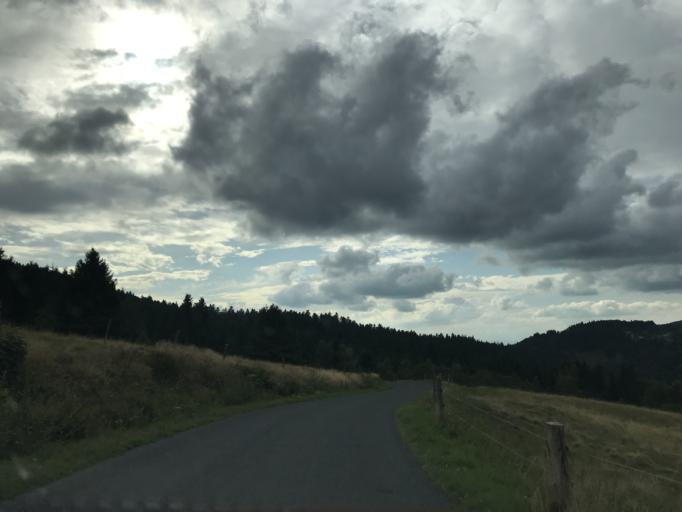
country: FR
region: Auvergne
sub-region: Departement du Puy-de-Dome
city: Job
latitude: 45.6645
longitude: 3.7635
